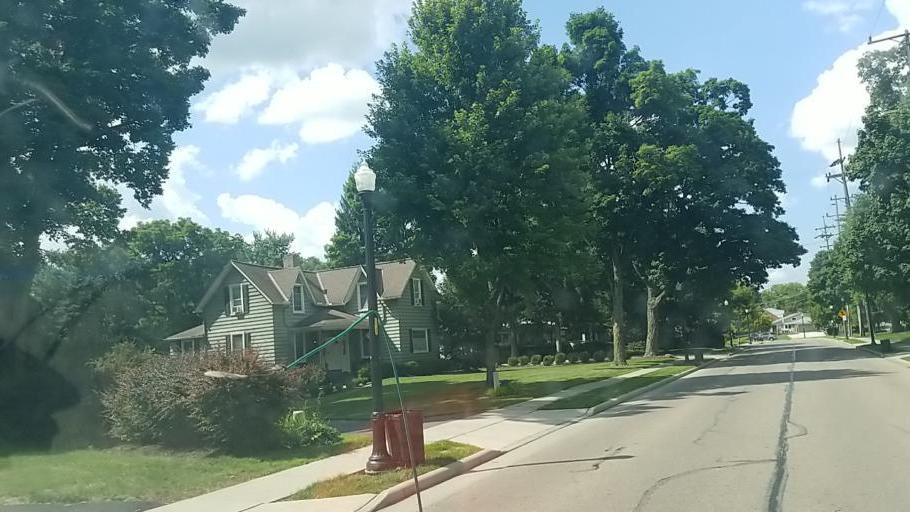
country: US
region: Ohio
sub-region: Franklin County
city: Westerville
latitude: 40.1280
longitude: -82.9395
